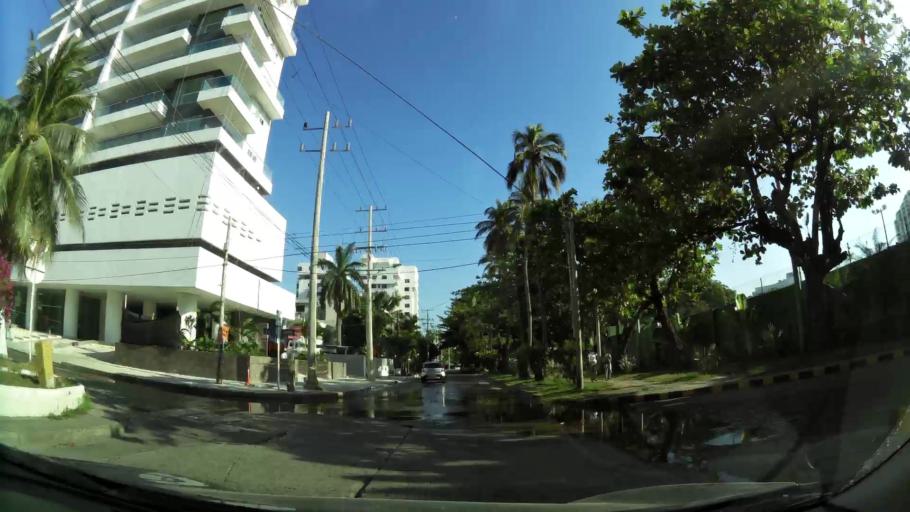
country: CO
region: Bolivar
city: Cartagena
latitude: 10.3972
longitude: -75.5592
